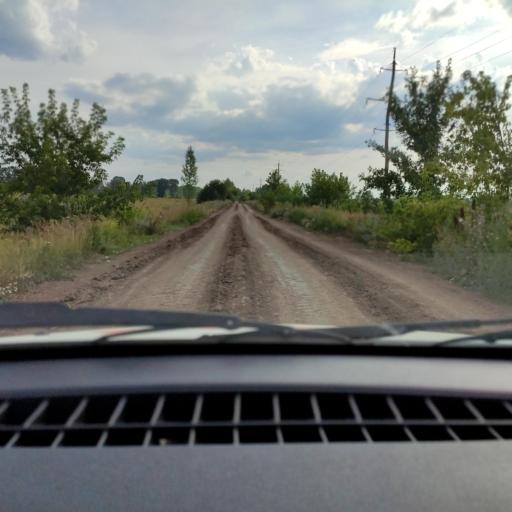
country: RU
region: Bashkortostan
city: Blagoveshchensk
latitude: 54.9253
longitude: 55.9443
